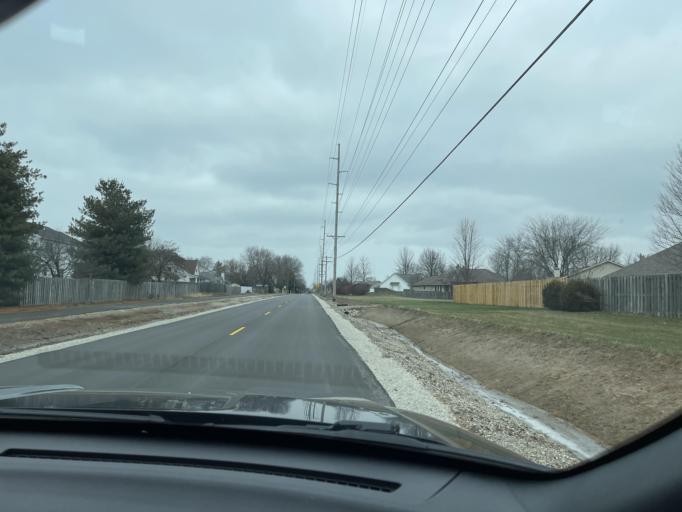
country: US
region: Illinois
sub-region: Sangamon County
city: Rochester
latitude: 39.7601
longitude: -89.5786
